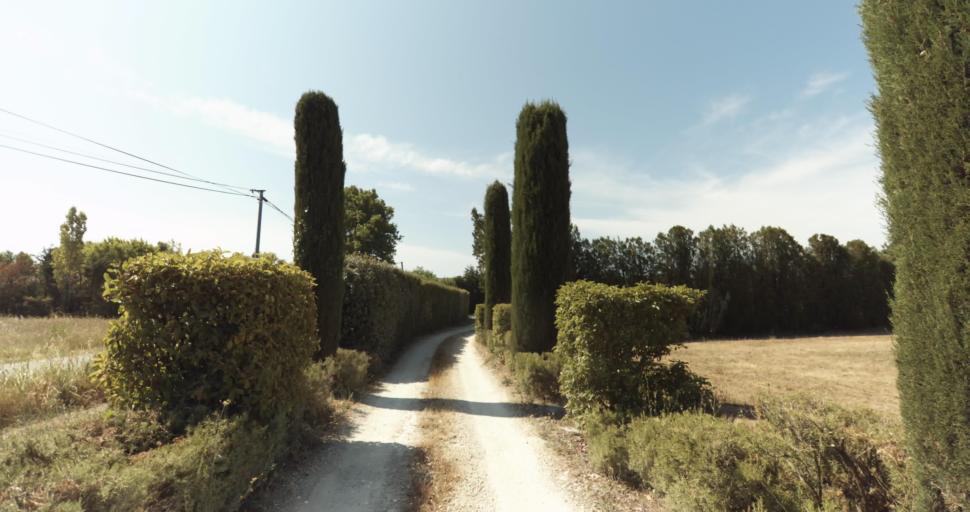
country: FR
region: Provence-Alpes-Cote d'Azur
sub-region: Departement du Vaucluse
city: Monteux
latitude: 44.0173
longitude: 4.9949
